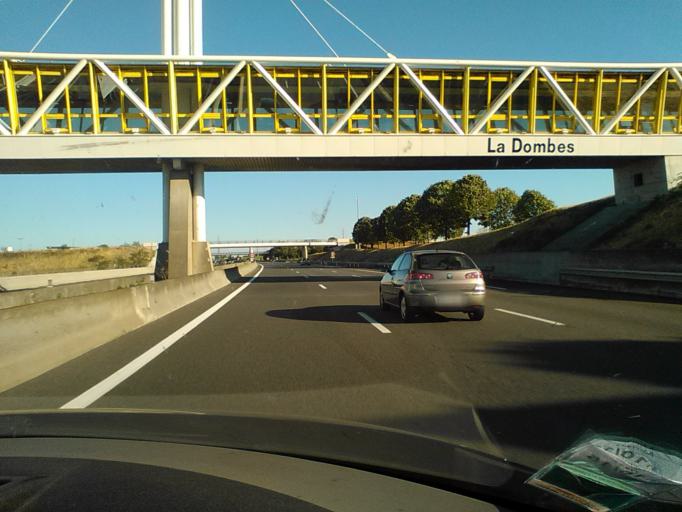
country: FR
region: Rhone-Alpes
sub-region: Departement du Rhone
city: Montanay
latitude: 45.8855
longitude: 4.8945
